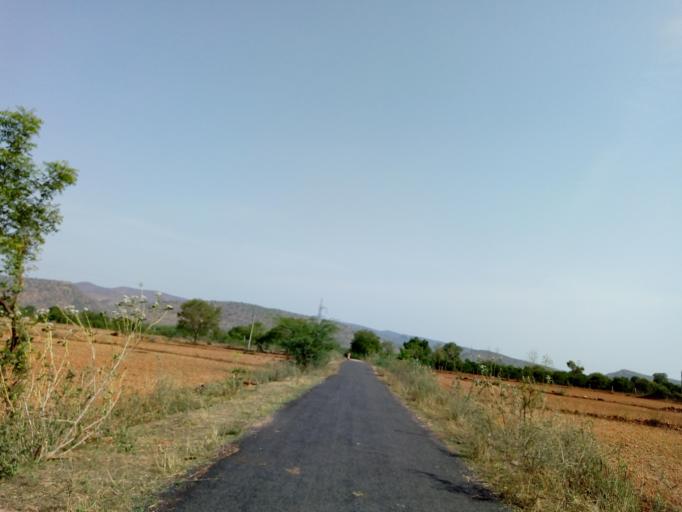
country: IN
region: Andhra Pradesh
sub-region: Prakasam
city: Cumbum
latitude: 15.7122
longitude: 79.0841
